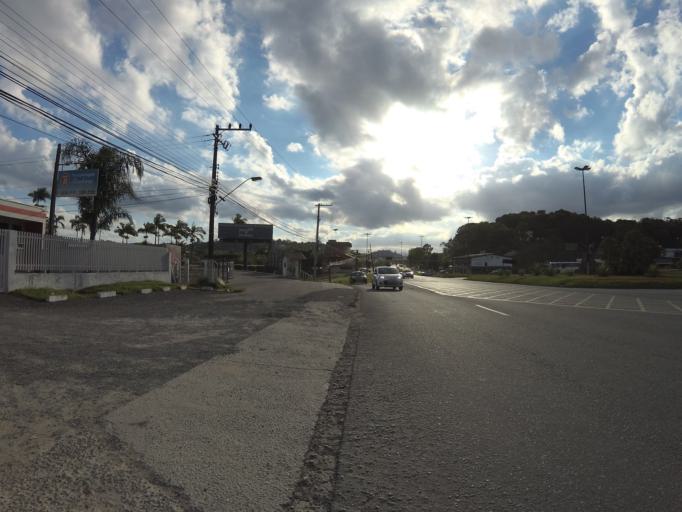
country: BR
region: Santa Catarina
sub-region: Blumenau
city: Blumenau
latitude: -26.8716
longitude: -49.0949
